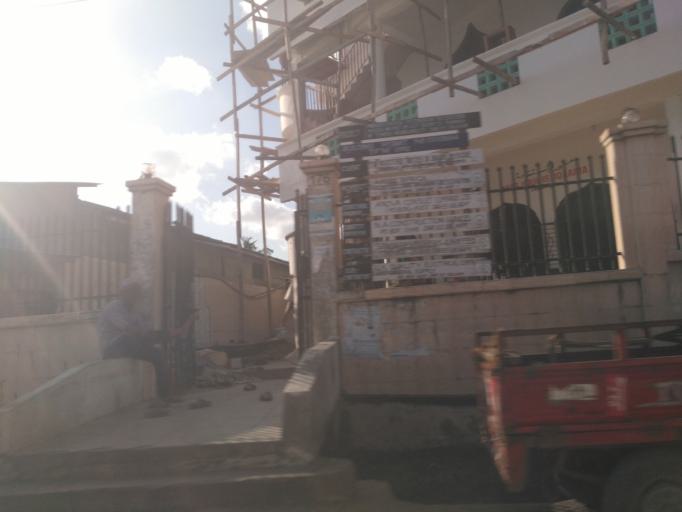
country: TZ
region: Dar es Salaam
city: Dar es Salaam
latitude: -6.8713
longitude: 39.2608
